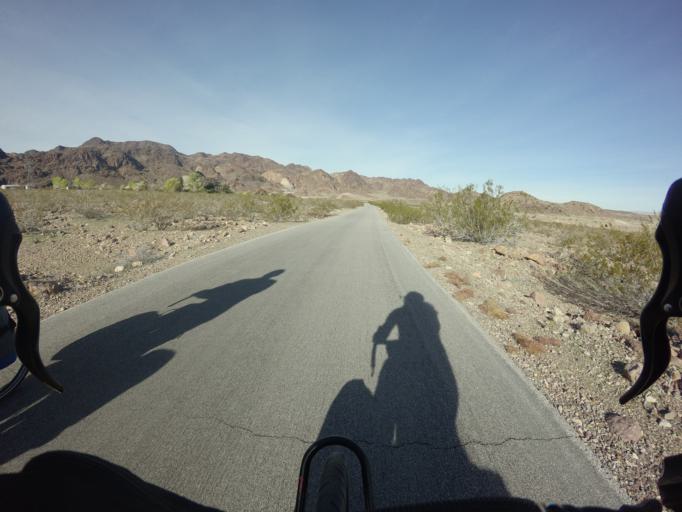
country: US
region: Nevada
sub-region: Clark County
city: Boulder City
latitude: 36.0450
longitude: -114.8106
